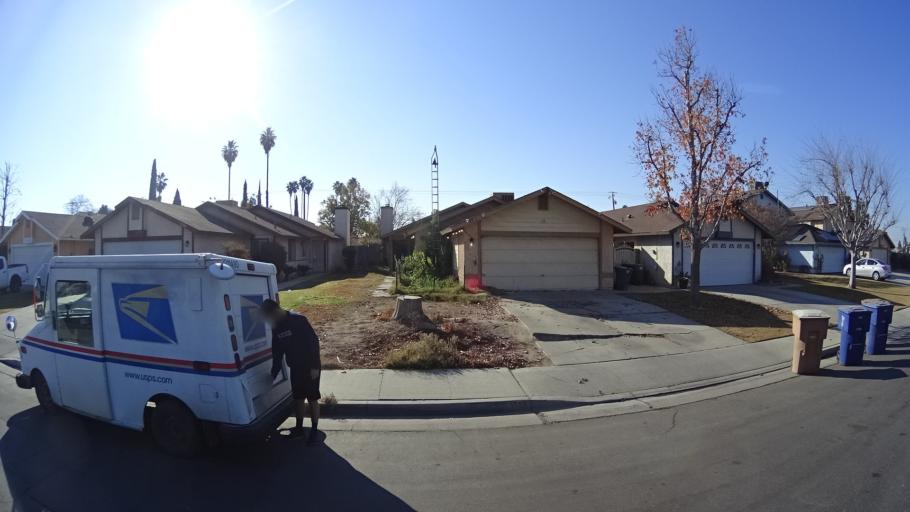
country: US
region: California
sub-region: Kern County
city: Greenfield
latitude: 35.3037
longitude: -119.0191
